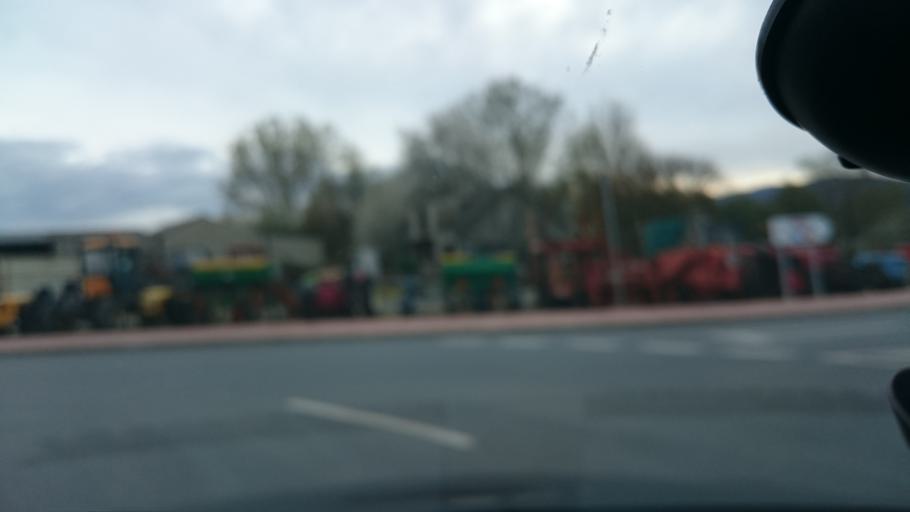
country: ES
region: Castille and Leon
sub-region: Provincia de Leon
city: Carracedelo
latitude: 42.5631
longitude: -6.7300
